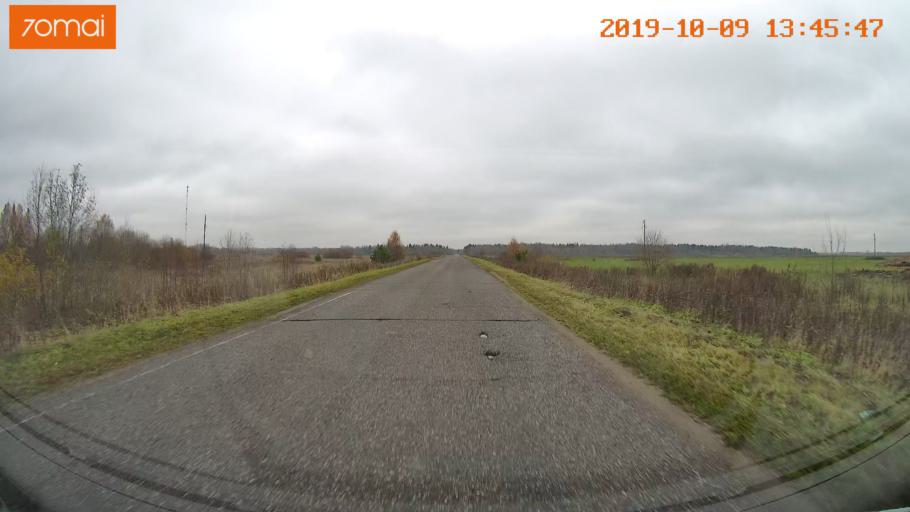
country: RU
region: Kostroma
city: Buy
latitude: 58.3775
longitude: 41.2127
